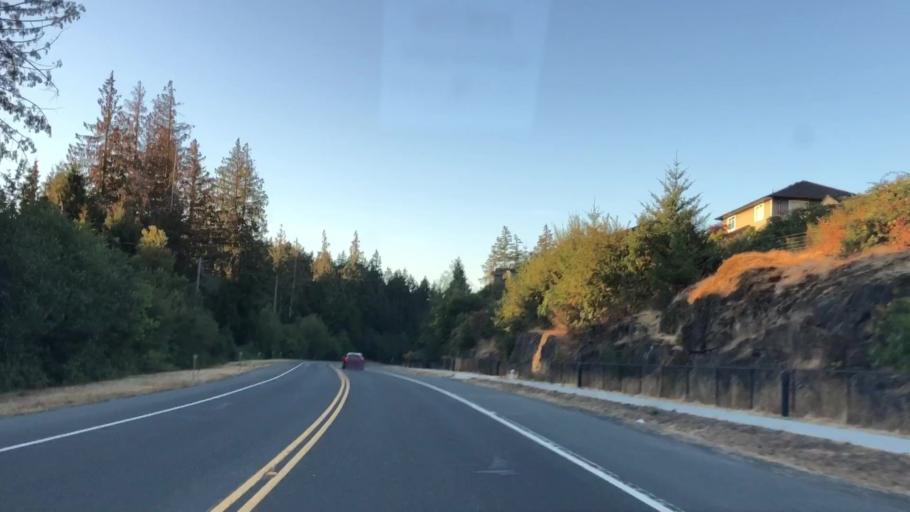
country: CA
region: British Columbia
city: Colwood
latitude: 48.4175
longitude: -123.5055
